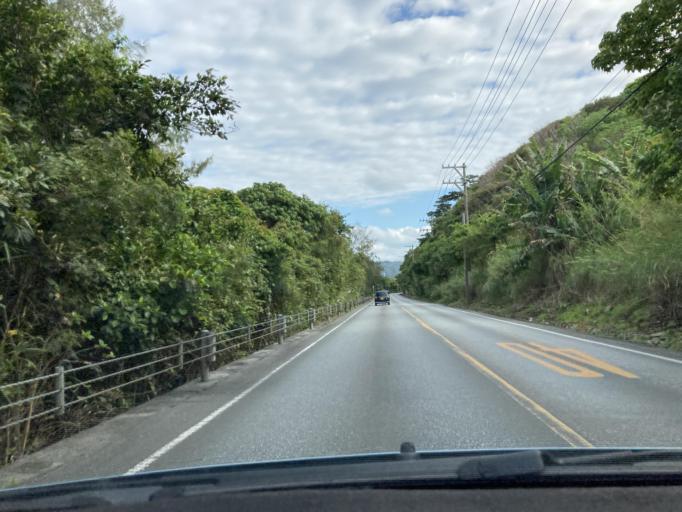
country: JP
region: Okinawa
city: Nago
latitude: 26.6425
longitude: 127.9993
